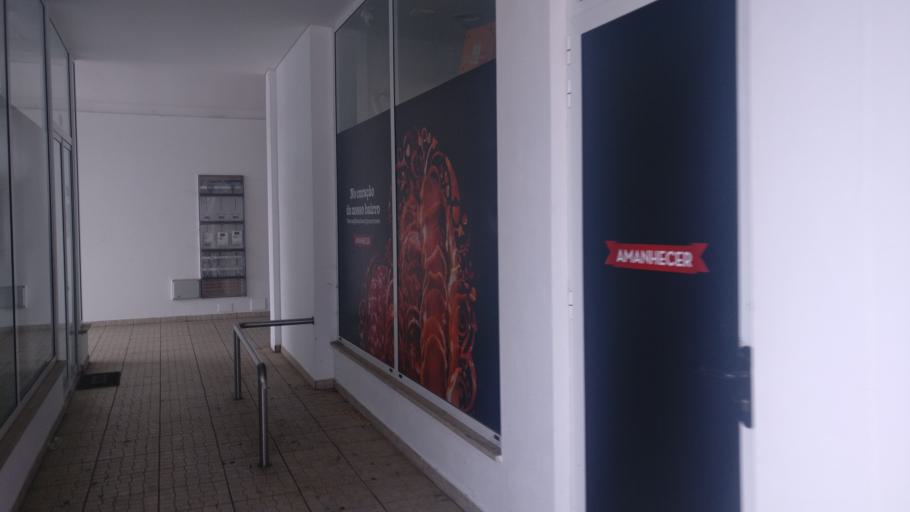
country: PT
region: Viseu
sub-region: Mortagua
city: Mortagua
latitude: 40.3965
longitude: -8.2285
